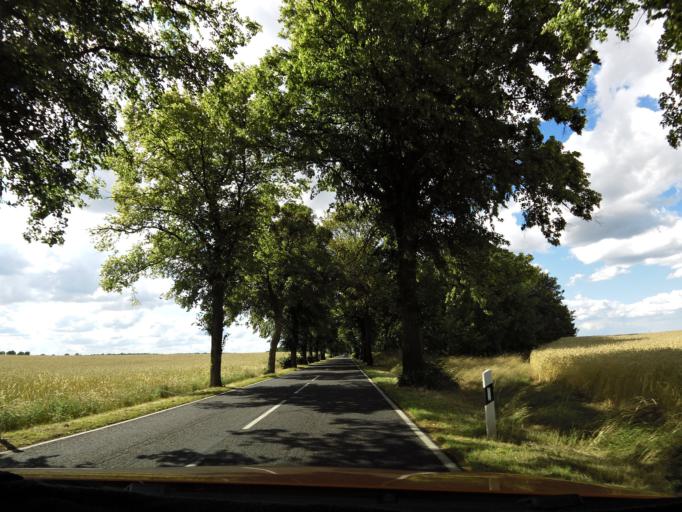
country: DE
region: Brandenburg
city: Mittenwalde
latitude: 52.2946
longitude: 13.5339
